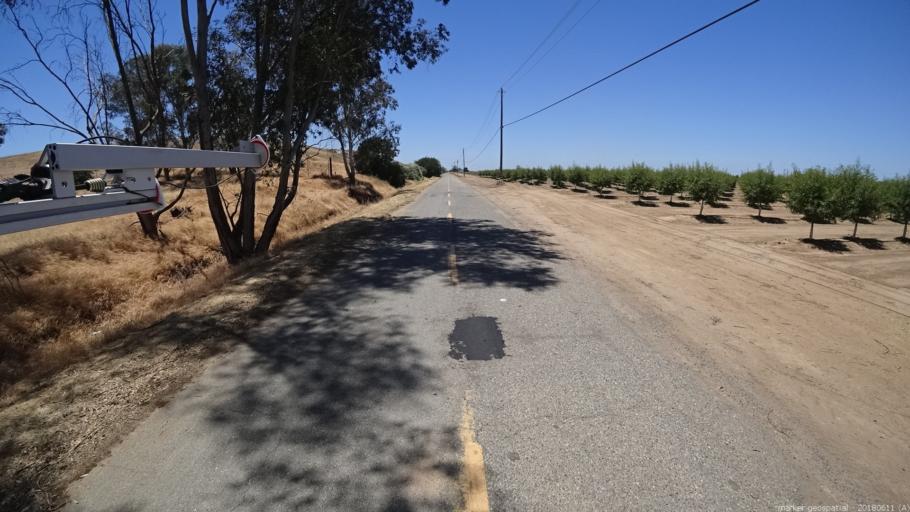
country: US
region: California
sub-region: Madera County
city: Fairmead
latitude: 37.0691
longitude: -120.1962
